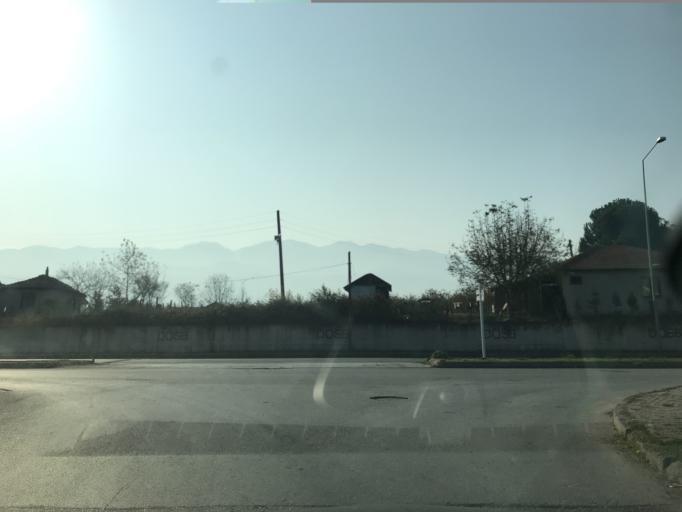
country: TR
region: Duzce
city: Duzce
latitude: 40.7835
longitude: 31.1536
